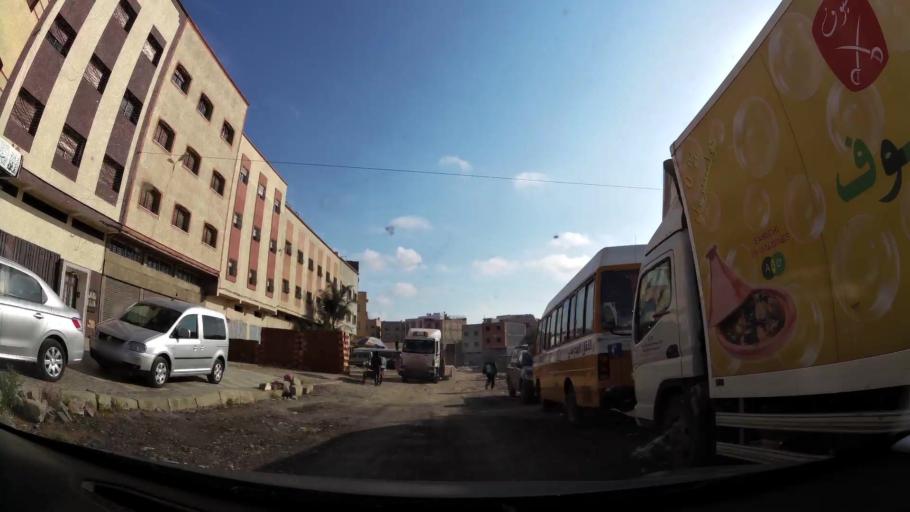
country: MA
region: Rabat-Sale-Zemmour-Zaer
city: Sale
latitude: 34.0559
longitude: -6.7753
